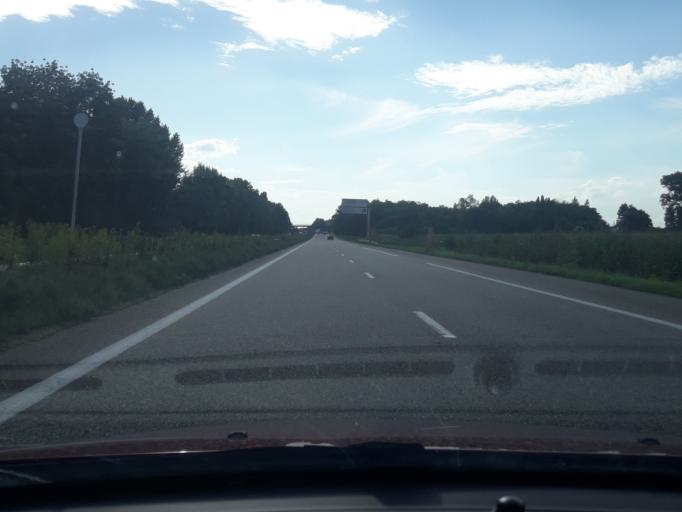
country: FR
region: Alsace
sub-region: Departement du Bas-Rhin
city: Hoerdt
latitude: 48.6781
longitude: 7.7887
